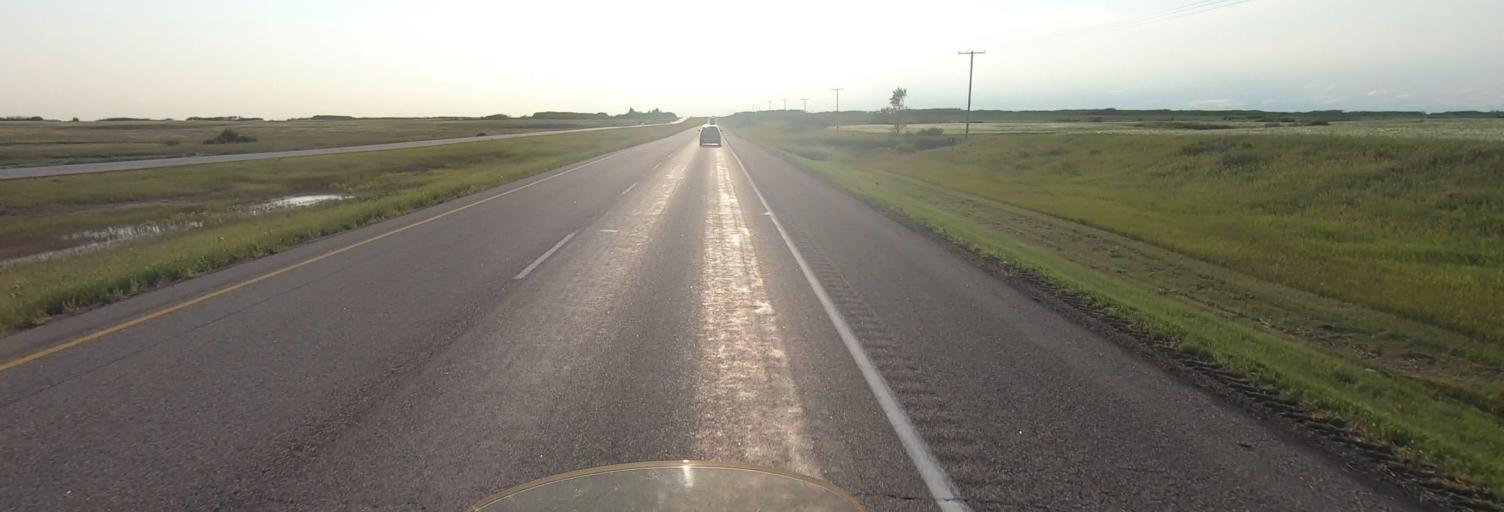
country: CA
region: Saskatchewan
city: Indian Head
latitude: 50.5278
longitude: -103.8000
